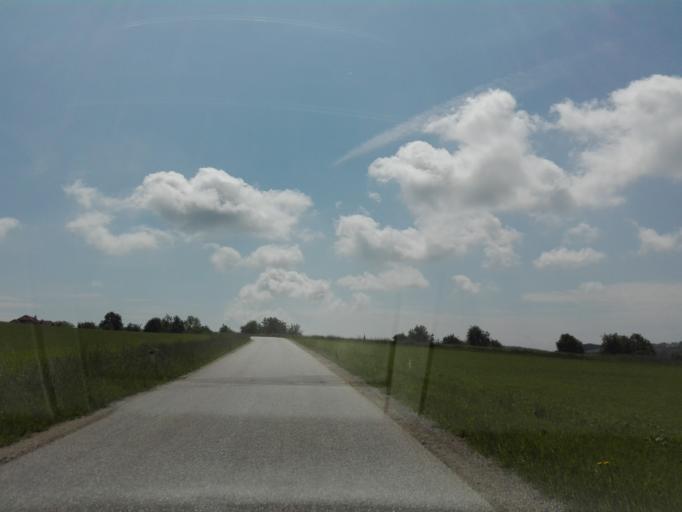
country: AT
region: Upper Austria
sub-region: Politischer Bezirk Rohrbach
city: Atzesberg
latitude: 48.4182
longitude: 13.9126
